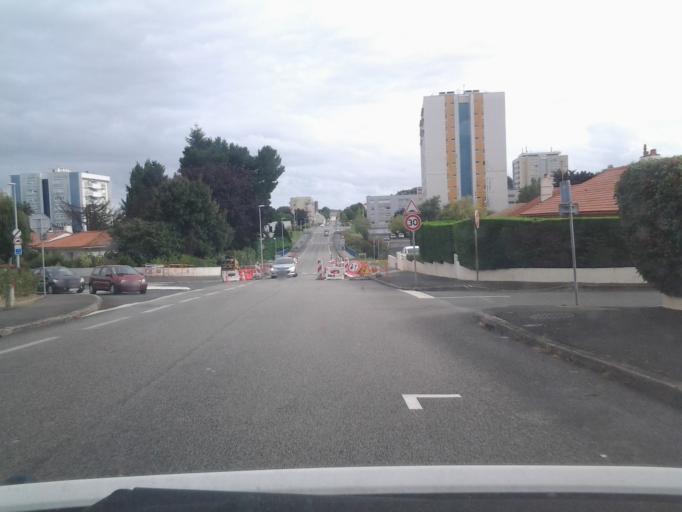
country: FR
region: Pays de la Loire
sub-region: Departement de la Vendee
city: La Roche-sur-Yon
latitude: 46.6822
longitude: -1.4221
